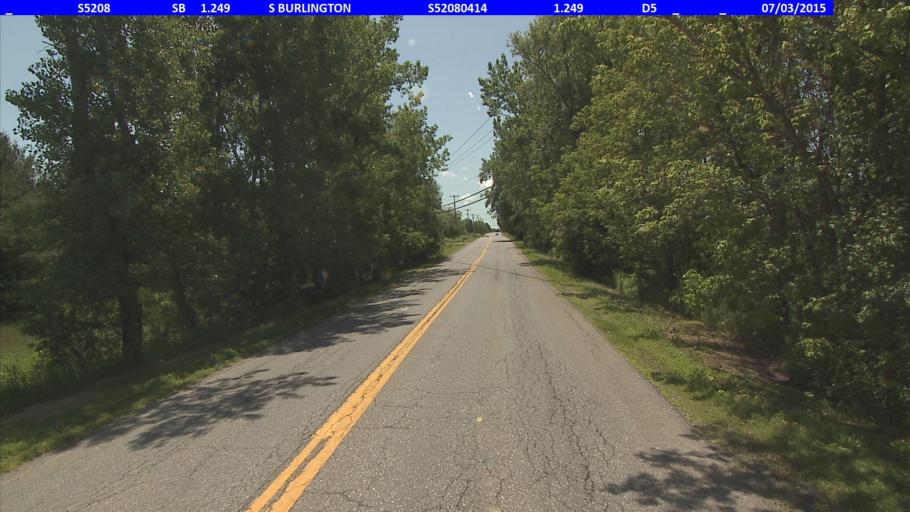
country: US
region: Vermont
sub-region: Chittenden County
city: South Burlington
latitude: 44.4287
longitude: -73.1748
